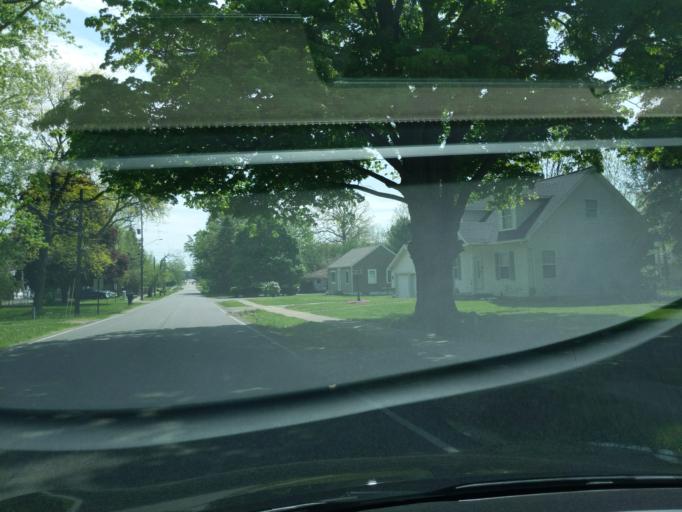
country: US
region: Michigan
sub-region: Ingham County
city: Holt
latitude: 42.6475
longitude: -84.5151
